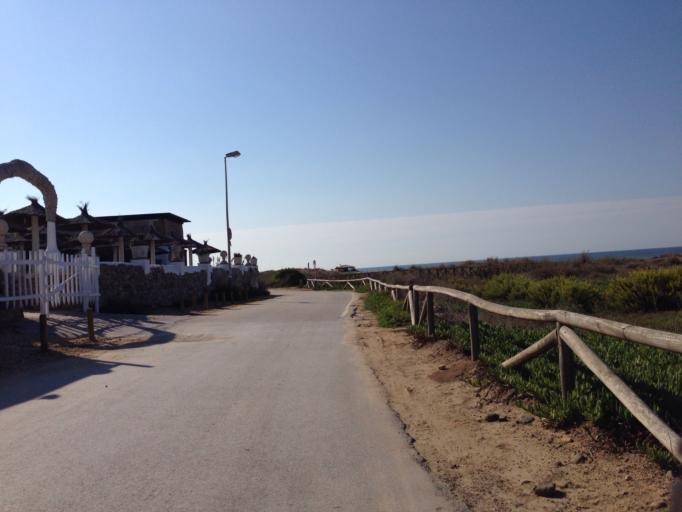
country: ES
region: Andalusia
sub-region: Provincia de Cadiz
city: Conil de la Frontera
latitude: 36.2191
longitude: -6.0615
